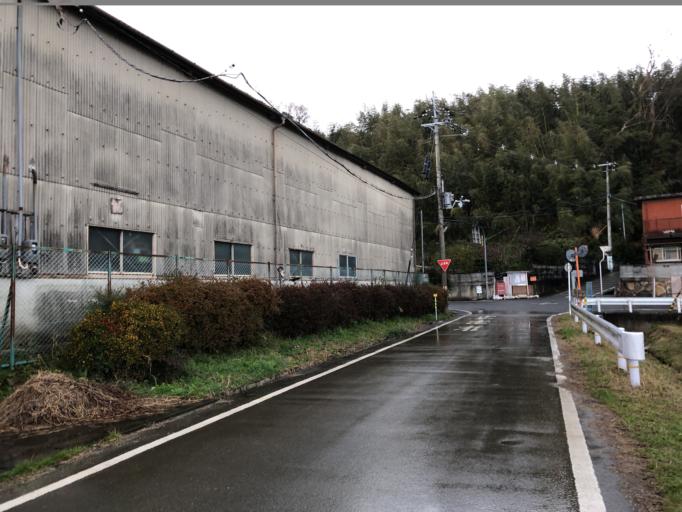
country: JP
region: Kyoto
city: Kameoka
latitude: 35.0204
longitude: 135.5947
